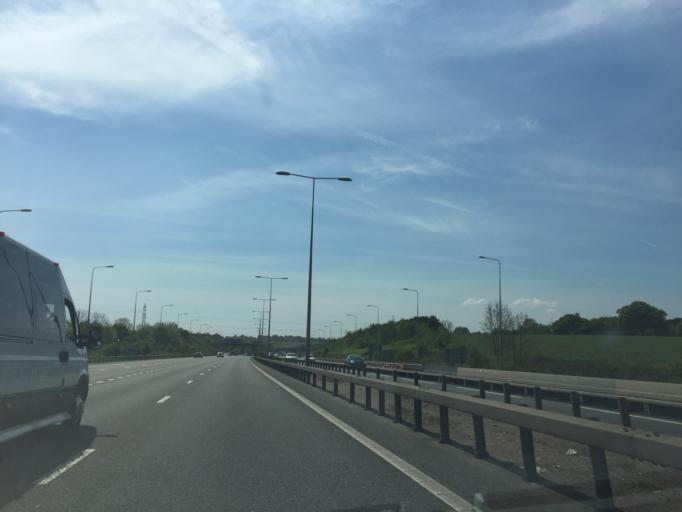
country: GB
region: England
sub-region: Essex
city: Epping
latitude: 51.6863
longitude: 0.1334
